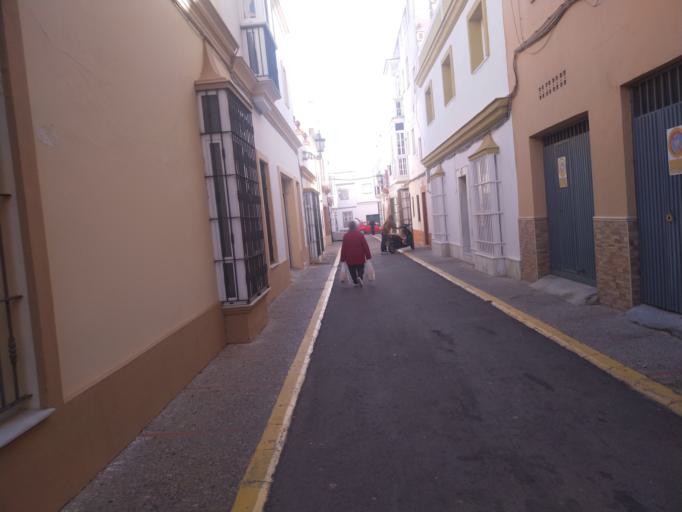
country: ES
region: Andalusia
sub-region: Provincia de Cadiz
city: San Fernando
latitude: 36.4704
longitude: -6.1948
